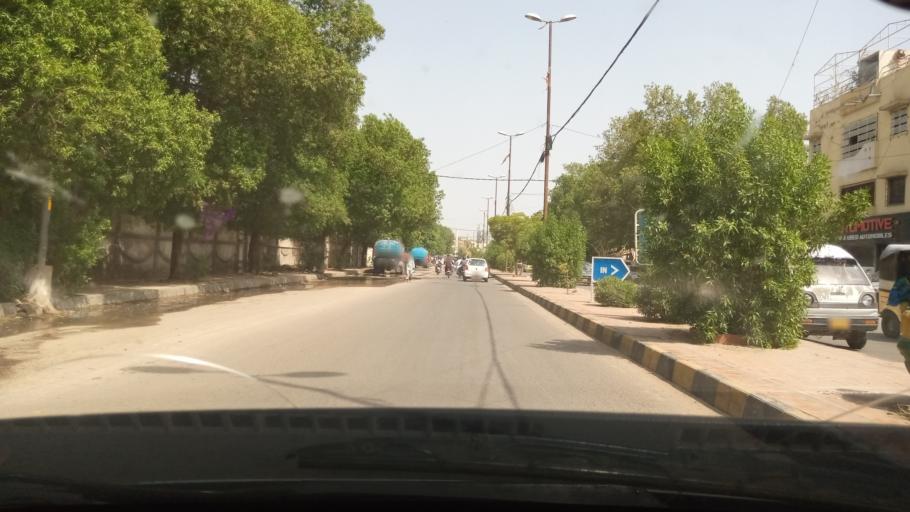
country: PK
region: Sindh
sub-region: Karachi District
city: Karachi
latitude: 24.8751
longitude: 67.0461
